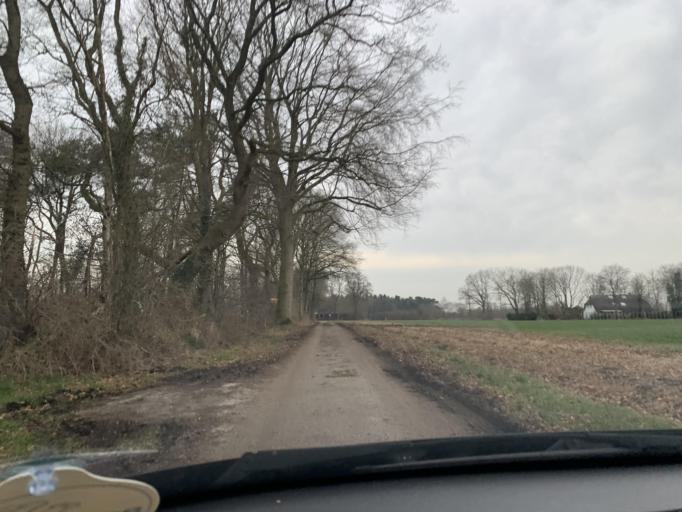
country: DE
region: Lower Saxony
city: Bad Zwischenahn
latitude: 53.2186
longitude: 7.9774
